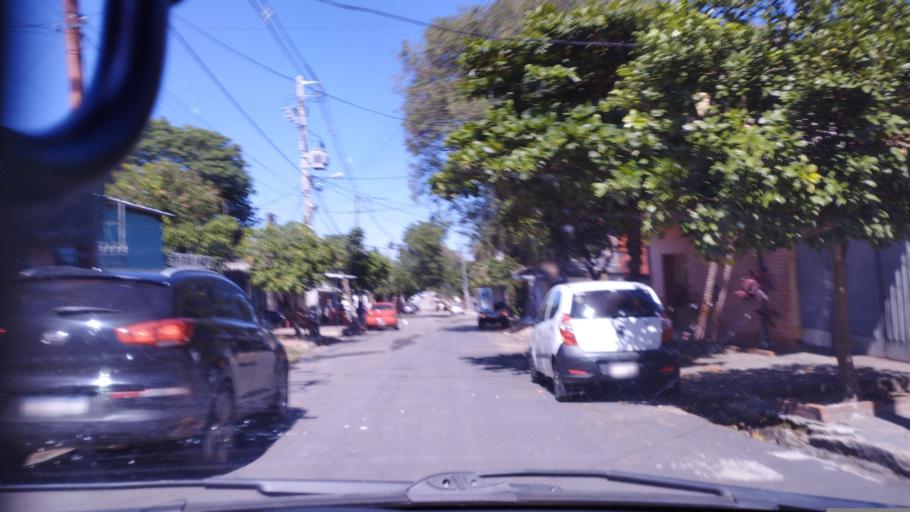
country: PY
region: Asuncion
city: Asuncion
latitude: -25.2961
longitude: -57.6650
